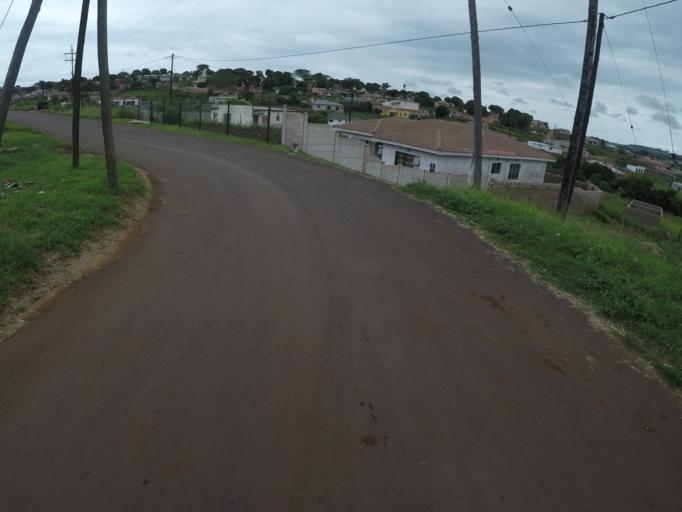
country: ZA
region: KwaZulu-Natal
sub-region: uThungulu District Municipality
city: Empangeni
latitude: -28.7758
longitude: 31.8574
